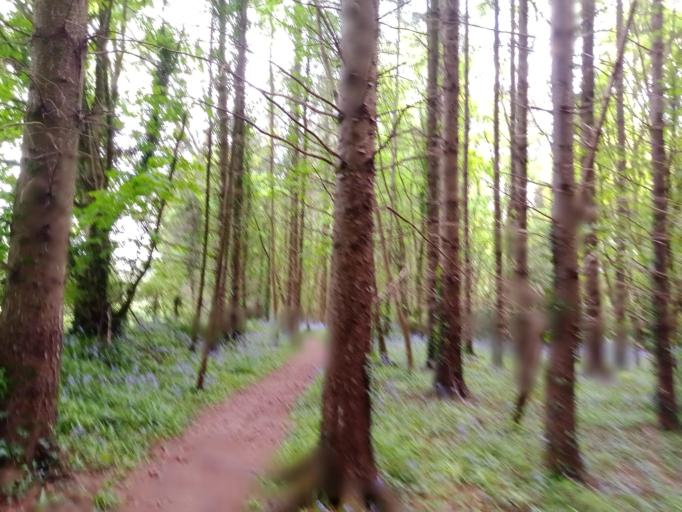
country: IE
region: Leinster
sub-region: Kilkenny
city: Castlecomer
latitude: 52.8192
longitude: -7.2047
